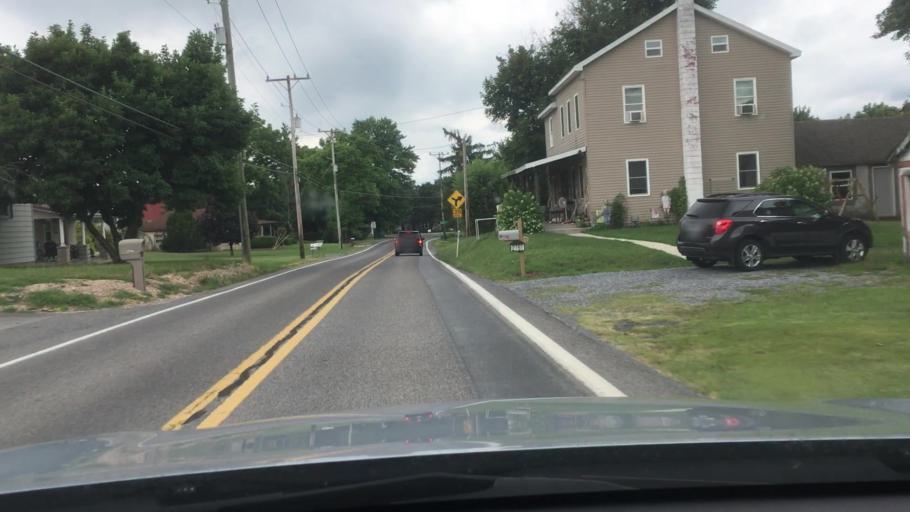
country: US
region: Pennsylvania
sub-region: Franklin County
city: Greencastle
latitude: 39.8715
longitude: -77.7310
